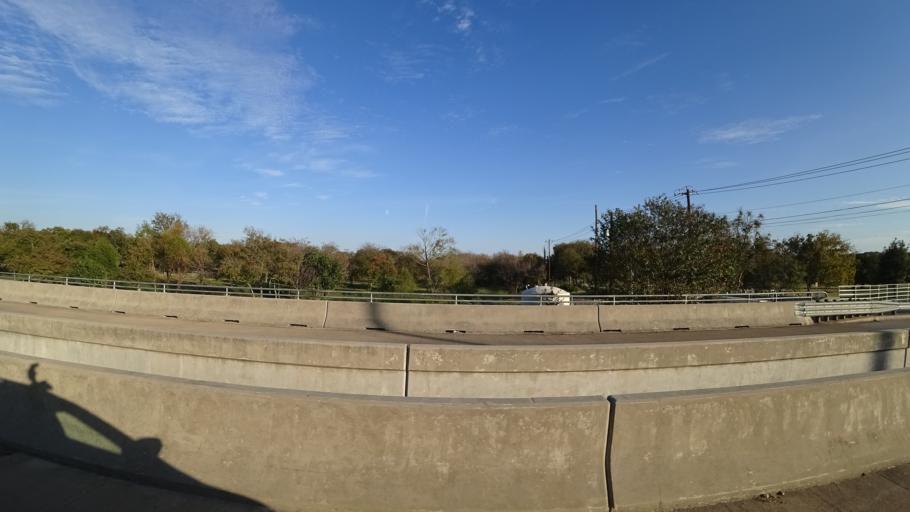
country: US
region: Texas
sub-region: Travis County
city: Pflugerville
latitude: 30.4192
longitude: -97.6458
